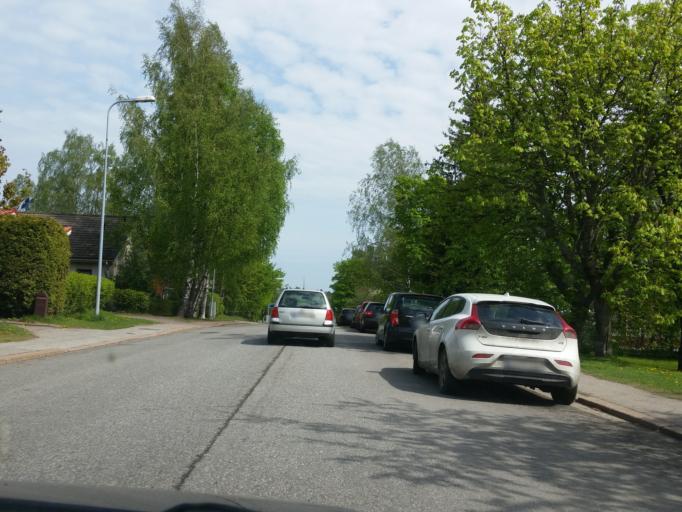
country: FI
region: Uusimaa
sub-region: Helsinki
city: Helsinki
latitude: 60.2393
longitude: 24.9402
